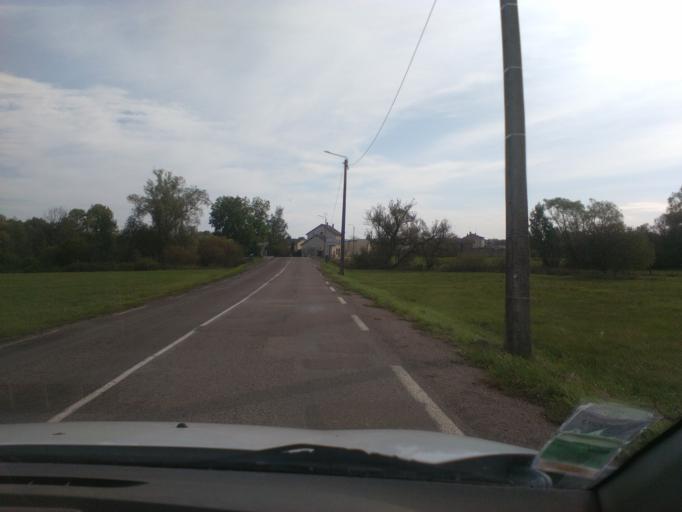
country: FR
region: Lorraine
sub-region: Departement des Vosges
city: Rambervillers
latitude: 48.3461
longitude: 6.6223
